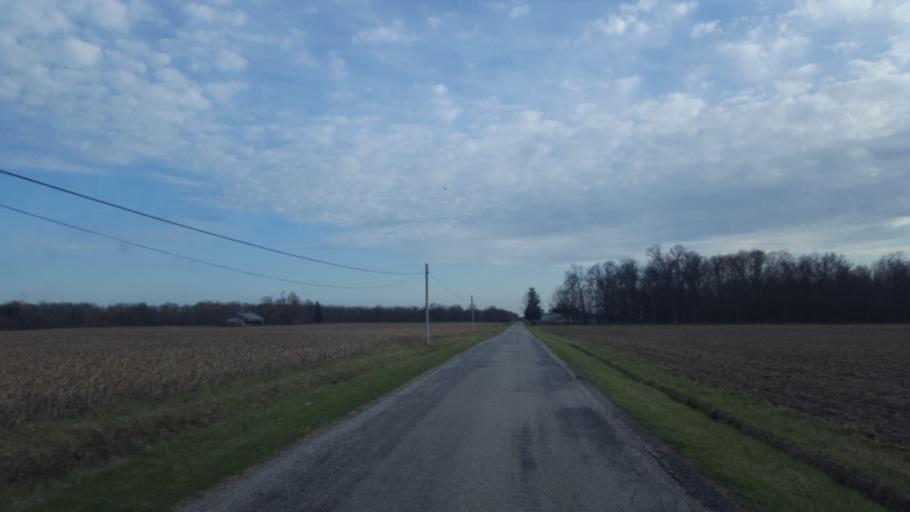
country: US
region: Ohio
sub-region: Crawford County
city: Bucyrus
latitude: 40.7026
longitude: -82.9483
